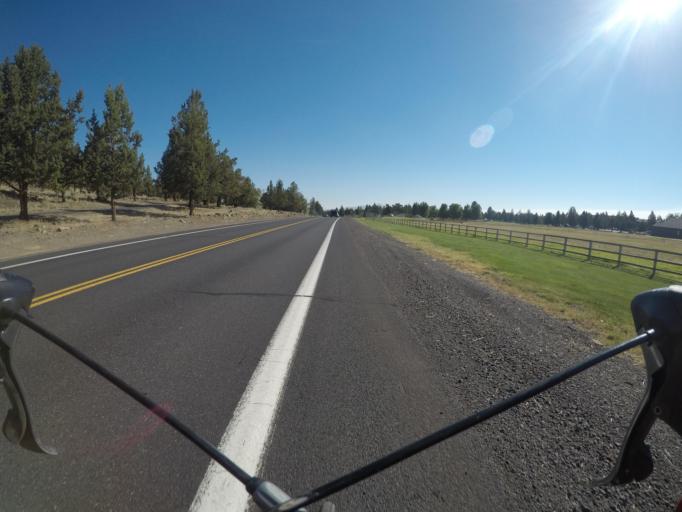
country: US
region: Oregon
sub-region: Deschutes County
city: Redmond
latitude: 44.2600
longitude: -121.2664
